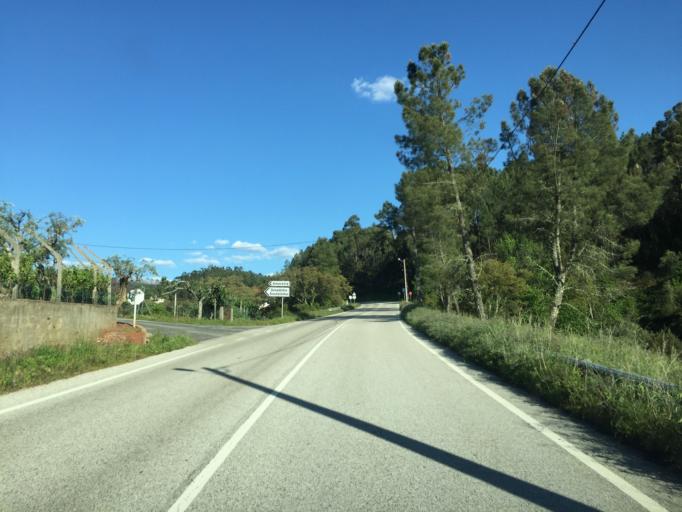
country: PT
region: Leiria
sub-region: Pedrogao Grande
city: Pedrogao Grande
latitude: 39.9863
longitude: -8.0715
